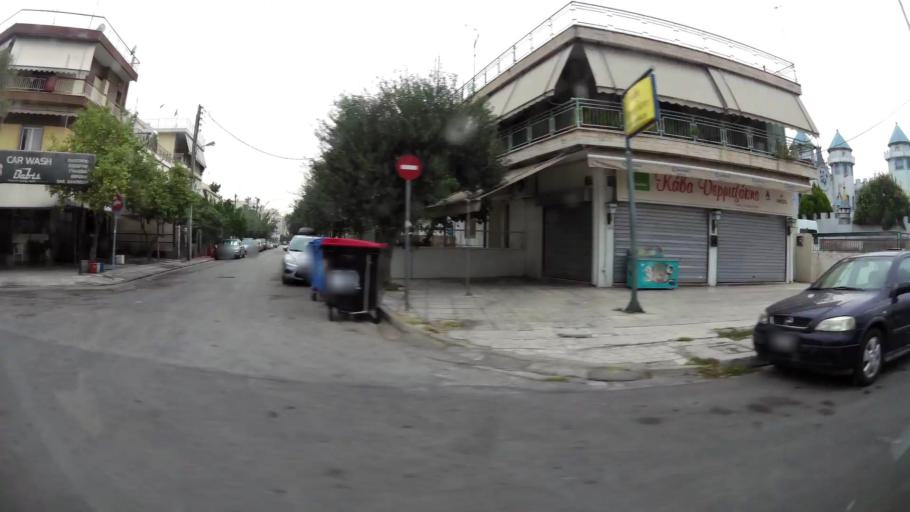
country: GR
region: Attica
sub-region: Nomarchia Athinas
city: Peristeri
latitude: 38.0090
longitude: 23.7039
